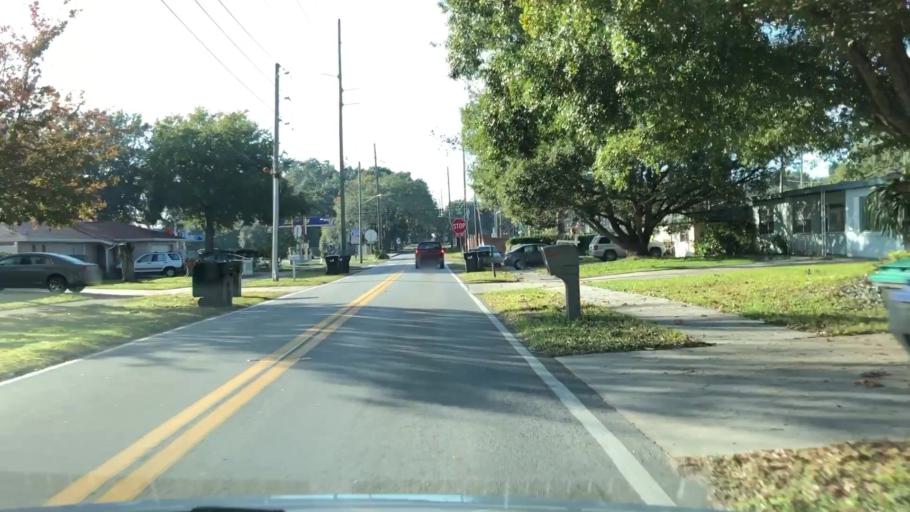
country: US
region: Florida
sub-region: Orange County
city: Conway
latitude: 28.5030
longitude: -81.3392
